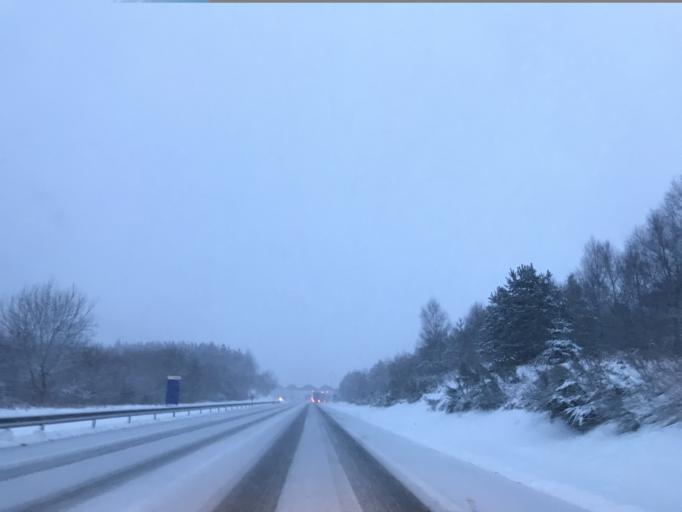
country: FR
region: Auvergne
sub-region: Departement du Puy-de-Dome
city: Saint-Sauves-d'Auvergne
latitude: 45.6628
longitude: 2.6848
